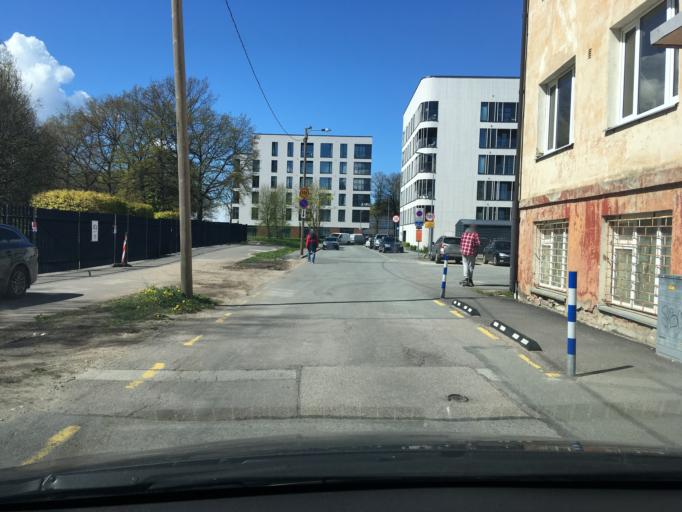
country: EE
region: Harju
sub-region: Tallinna linn
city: Tallinn
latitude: 59.4269
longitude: 24.7651
